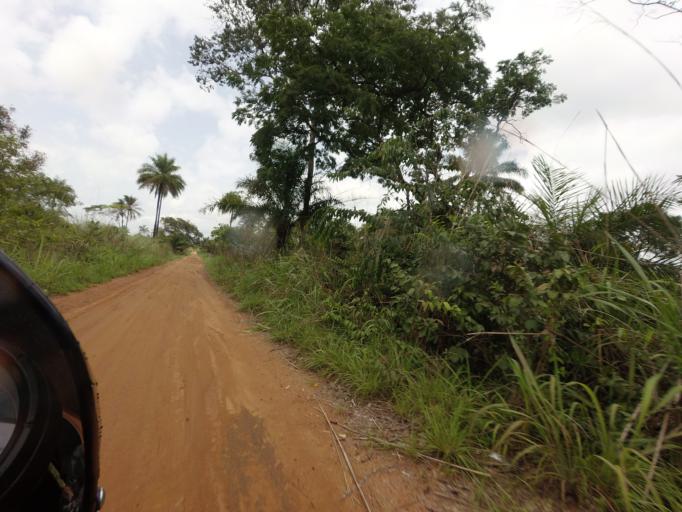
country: SL
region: Northern Province
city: Kassiri
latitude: 9.0234
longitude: -13.0566
